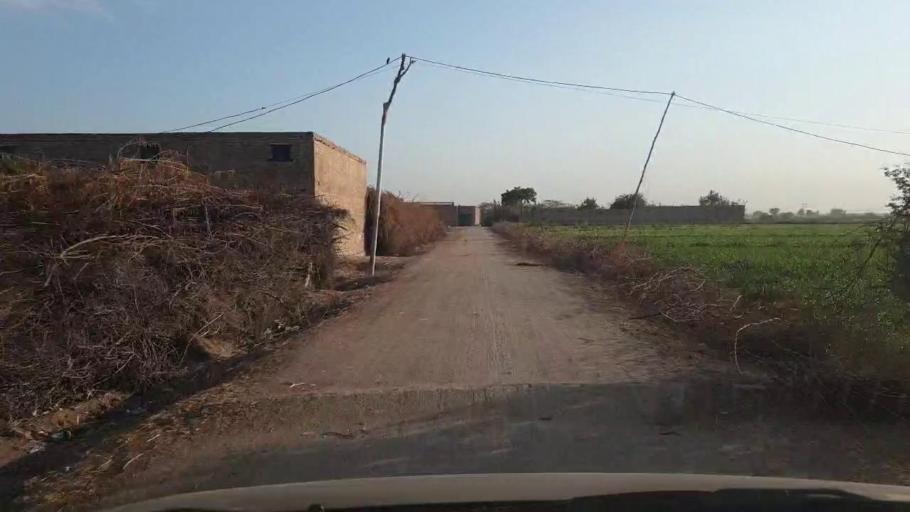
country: PK
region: Sindh
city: Sakrand
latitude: 26.0263
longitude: 68.3916
